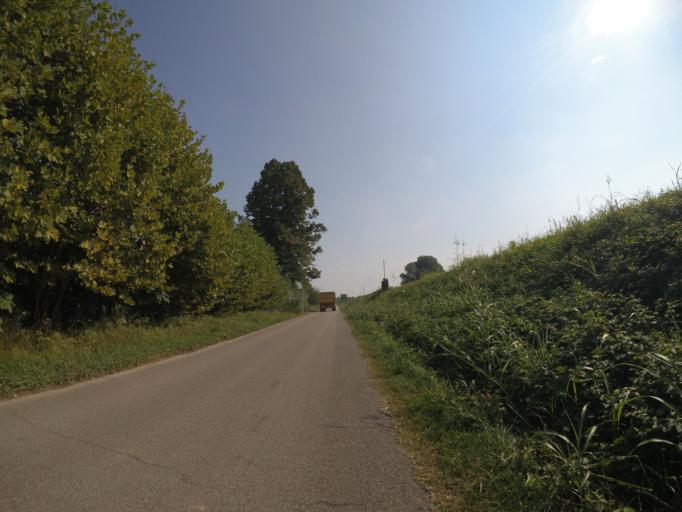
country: IT
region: Friuli Venezia Giulia
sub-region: Provincia di Udine
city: Camino al Tagliamento
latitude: 45.9026
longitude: 12.9378
